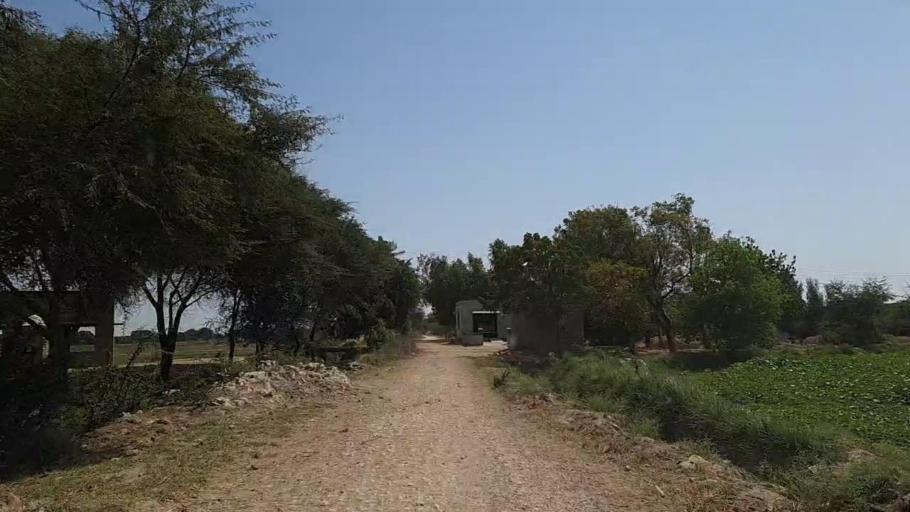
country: PK
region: Sindh
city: Mirpur Batoro
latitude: 24.7763
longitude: 68.2415
